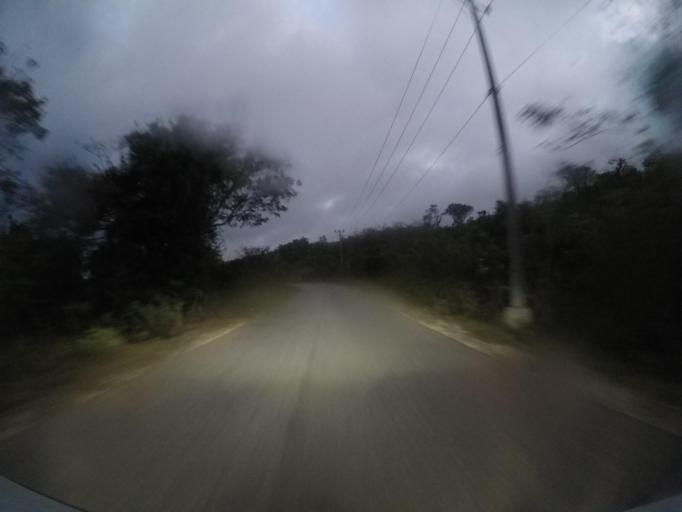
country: TL
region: Lautem
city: Lospalos
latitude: -8.4094
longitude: 126.9990
